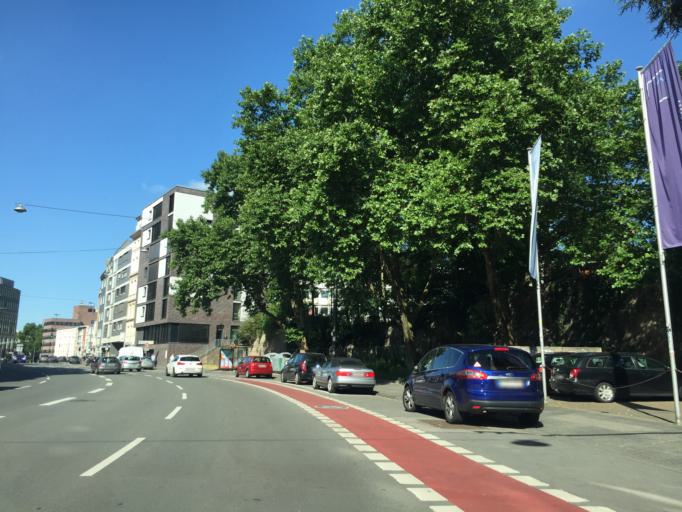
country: DE
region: North Rhine-Westphalia
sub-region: Regierungsbezirk Koln
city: Altstadt Sud
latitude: 50.9335
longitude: 6.9582
